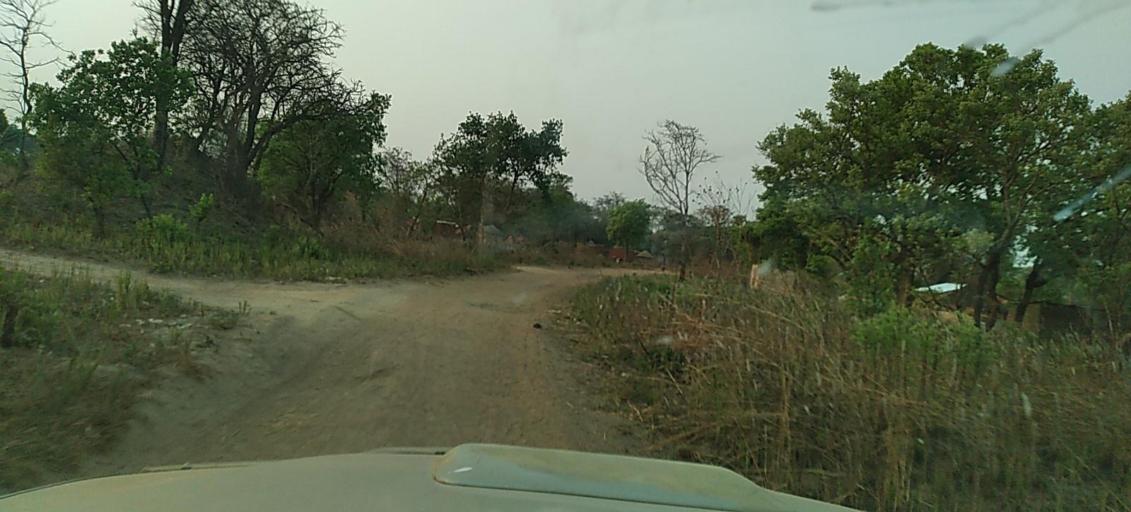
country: ZM
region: North-Western
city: Kasempa
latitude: -13.0686
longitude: 26.3808
